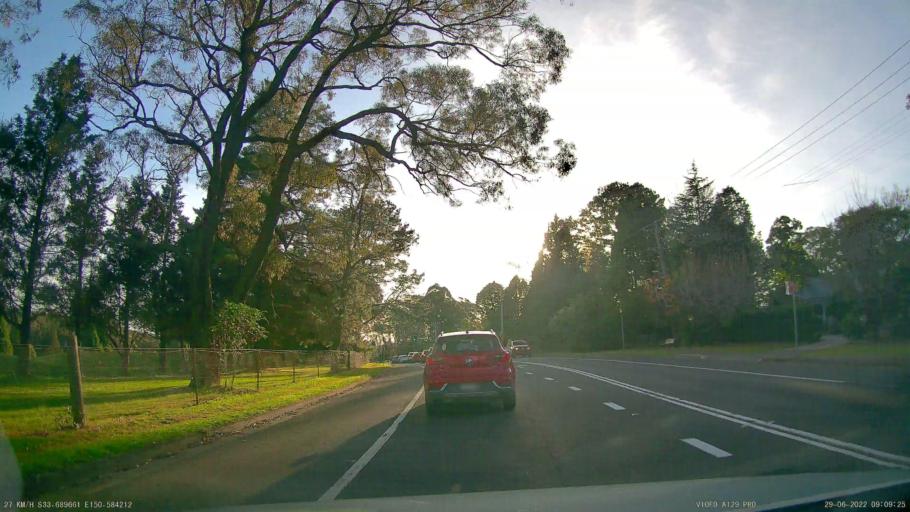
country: AU
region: New South Wales
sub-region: Blue Mountains Municipality
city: Blaxland
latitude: -33.6895
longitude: 150.5843
